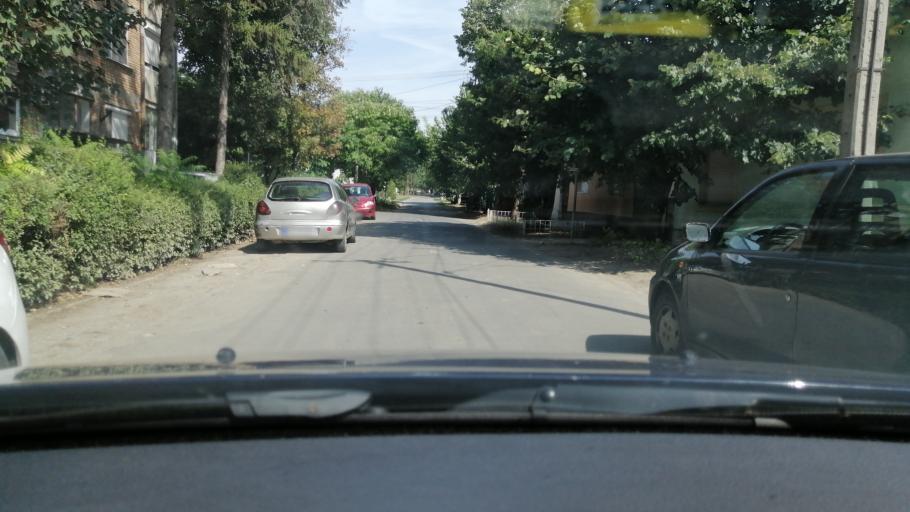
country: RS
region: Autonomna Pokrajina Vojvodina
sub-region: Srednjebanatski Okrug
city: Zrenjanin
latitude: 45.3901
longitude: 20.3752
